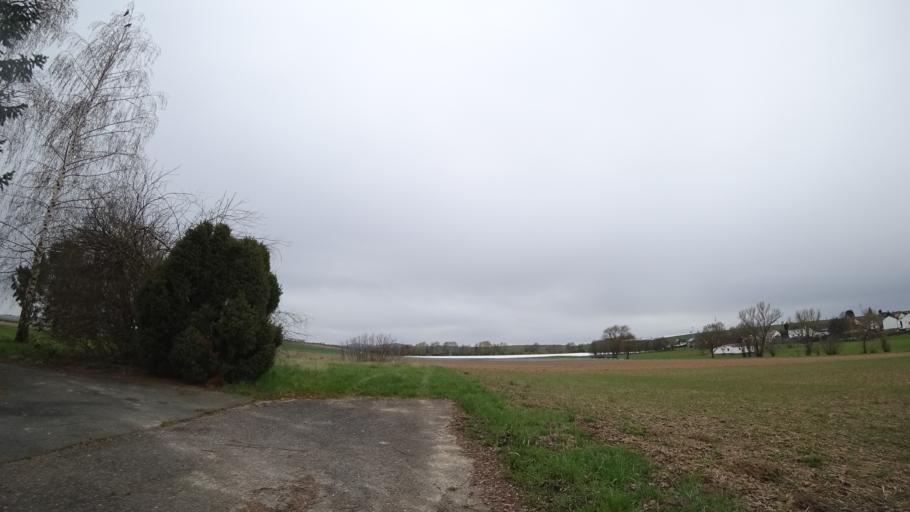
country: DE
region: Hesse
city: Grebenstein
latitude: 51.4227
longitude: 9.4319
